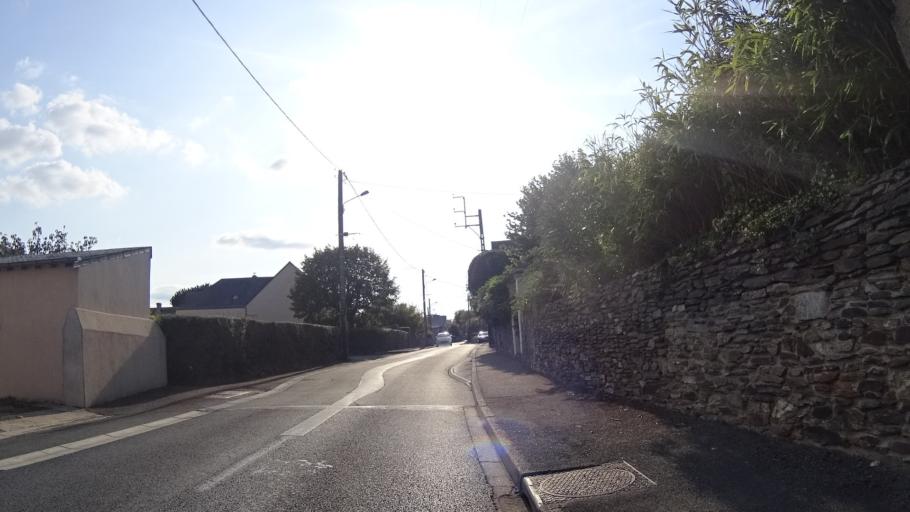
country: FR
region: Pays de la Loire
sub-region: Departement de Maine-et-Loire
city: Savennieres
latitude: 47.3973
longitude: -0.6351
